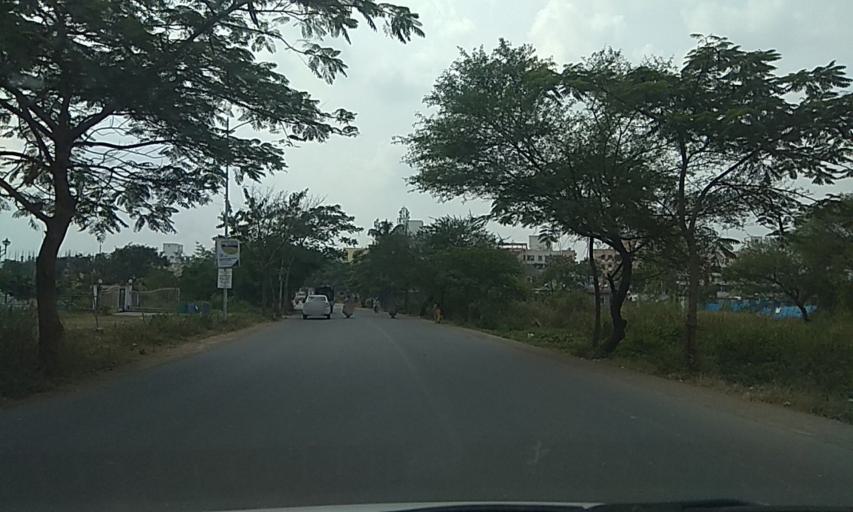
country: IN
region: Maharashtra
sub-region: Pune Division
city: Pimpri
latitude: 18.5774
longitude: 73.7130
